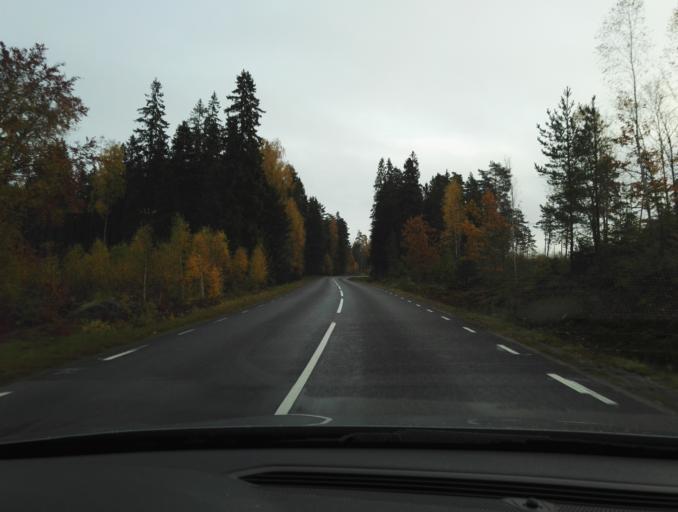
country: SE
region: Kronoberg
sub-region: Vaxjo Kommun
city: Rottne
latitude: 57.0076
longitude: 14.7632
